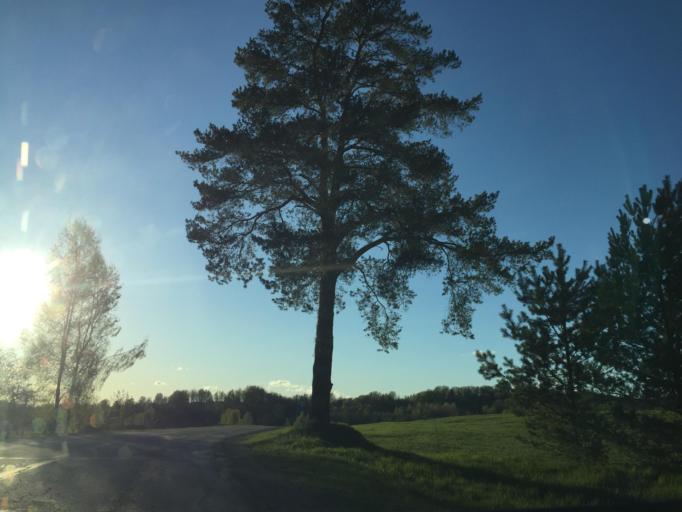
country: LV
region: Vecpiebalga
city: Vecpiebalga
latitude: 56.8662
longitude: 25.8390
